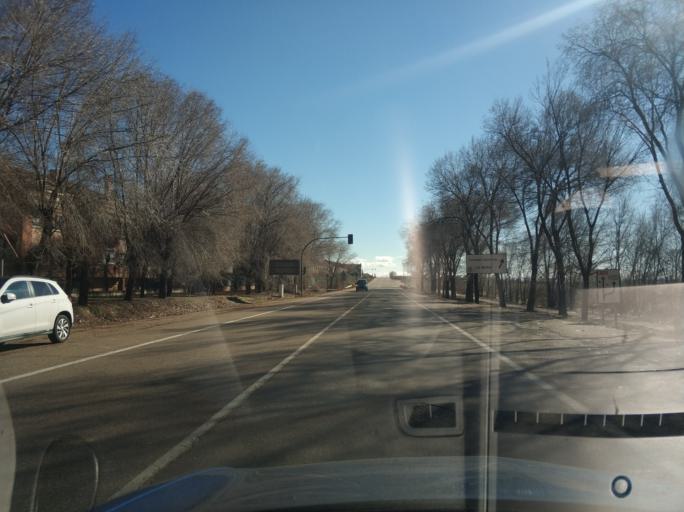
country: ES
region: Castille and Leon
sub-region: Provincia de Valladolid
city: Cisterniga
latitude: 41.6080
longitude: -4.6832
